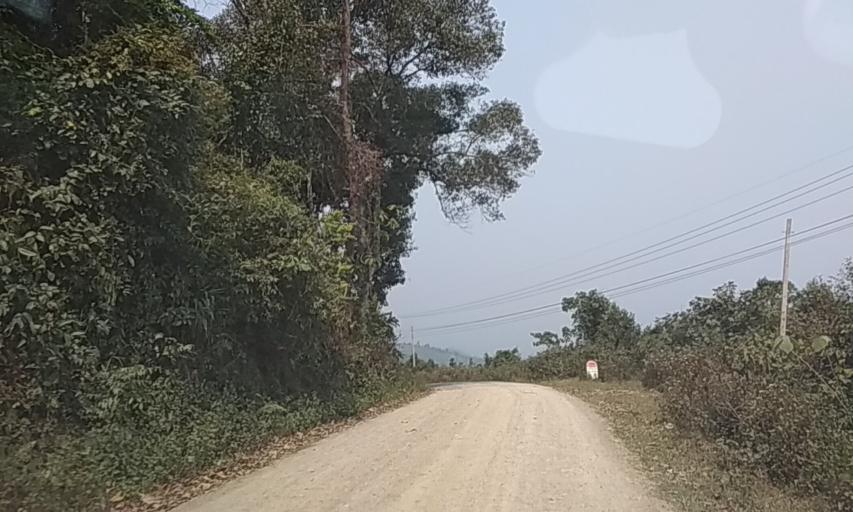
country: TH
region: Nan
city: Chaloem Phra Kiat
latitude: 20.0429
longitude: 101.0972
